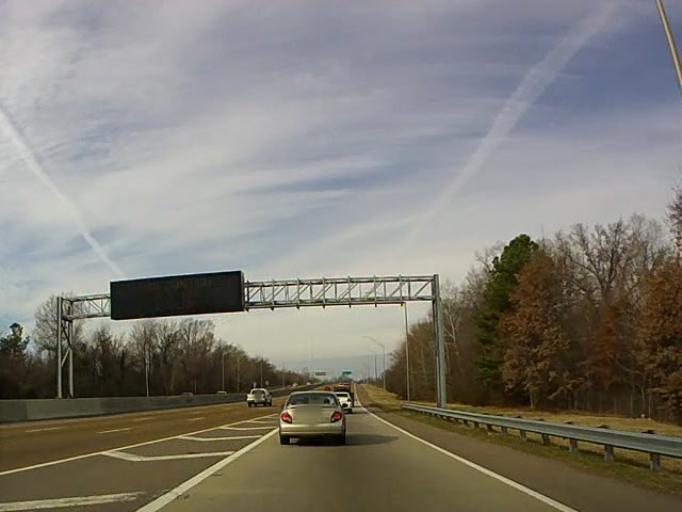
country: US
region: Tennessee
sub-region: Shelby County
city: Germantown
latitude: 35.0692
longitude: -89.8497
